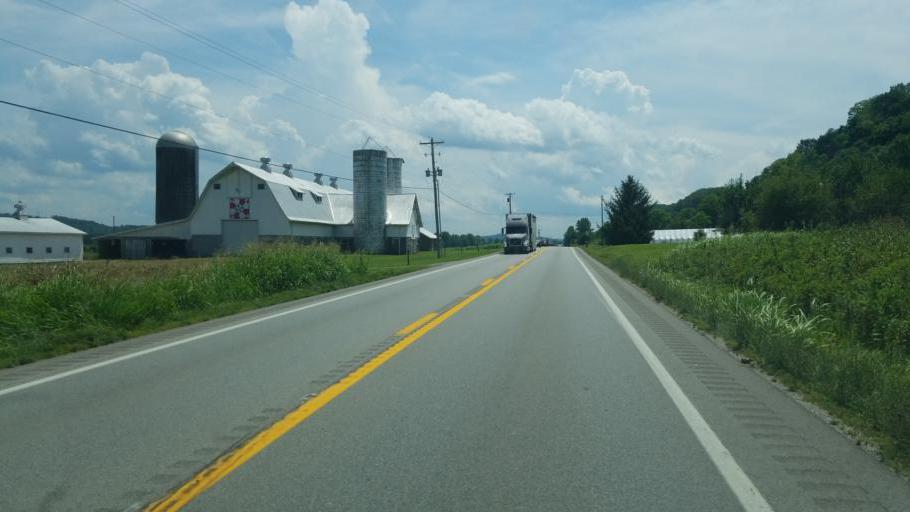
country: US
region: West Virginia
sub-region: Putnam County
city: Buffalo
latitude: 38.7279
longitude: -81.9723
